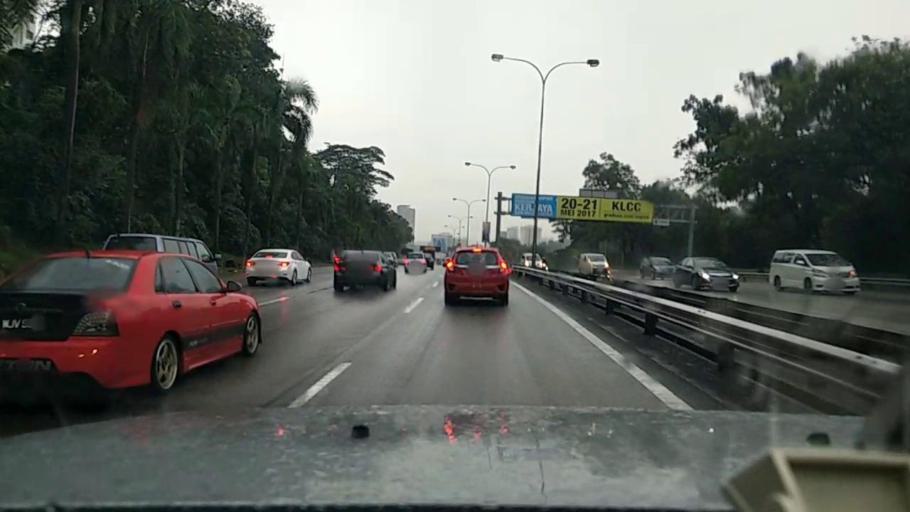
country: MY
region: Kuala Lumpur
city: Kuala Lumpur
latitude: 3.1087
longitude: 101.6914
